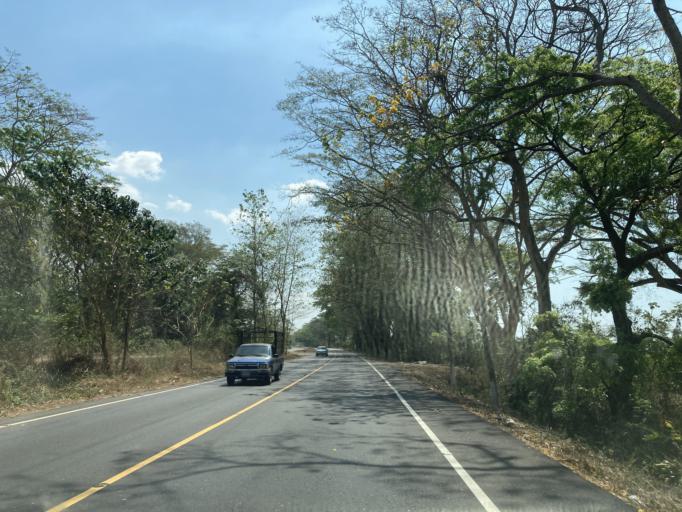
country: GT
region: Escuintla
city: Guanagazapa
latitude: 14.1791
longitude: -90.6871
